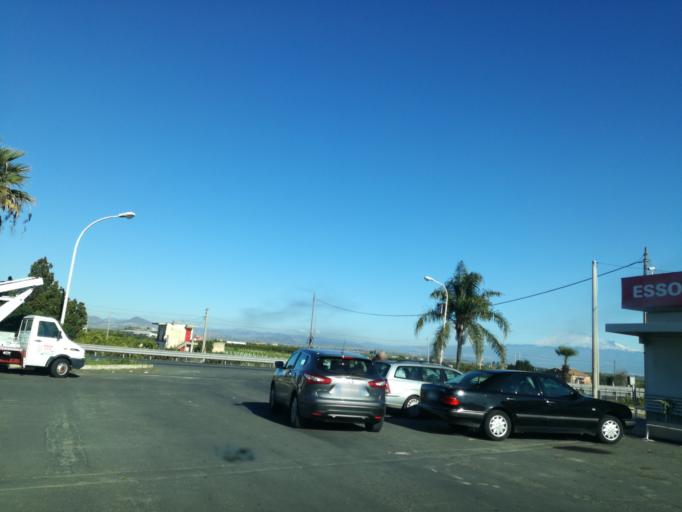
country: IT
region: Sicily
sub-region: Catania
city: Palagonia
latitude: 37.3788
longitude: 14.7490
